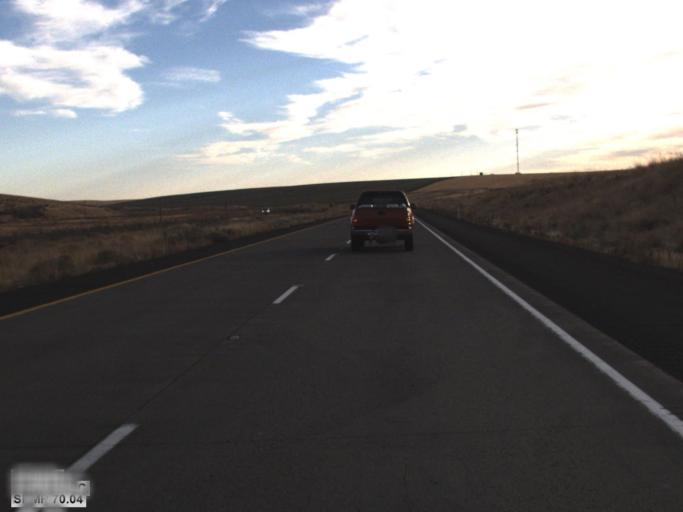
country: US
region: Washington
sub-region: Franklin County
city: Connell
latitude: 46.8198
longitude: -118.6850
